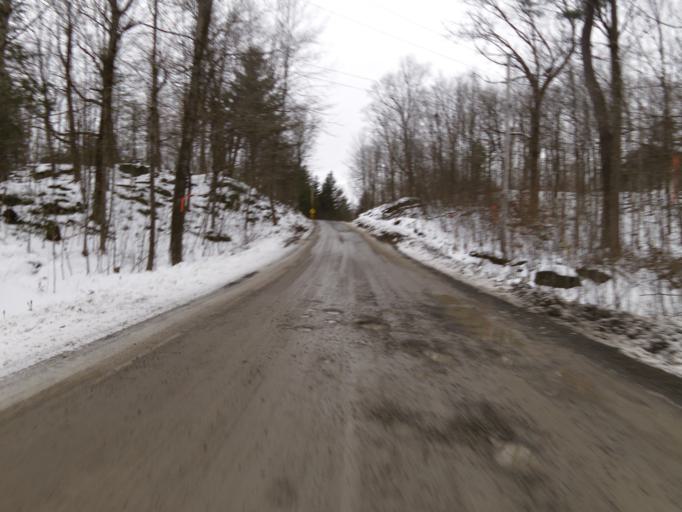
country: CA
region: Ontario
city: Carleton Place
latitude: 45.1712
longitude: -76.2315
